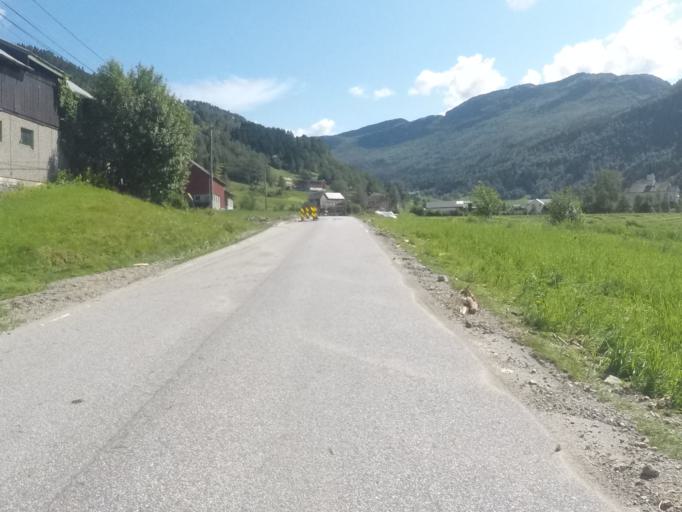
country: NO
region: Sogn og Fjordane
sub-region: Hoyanger
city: Hoyanger
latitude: 61.4210
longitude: 6.1532
